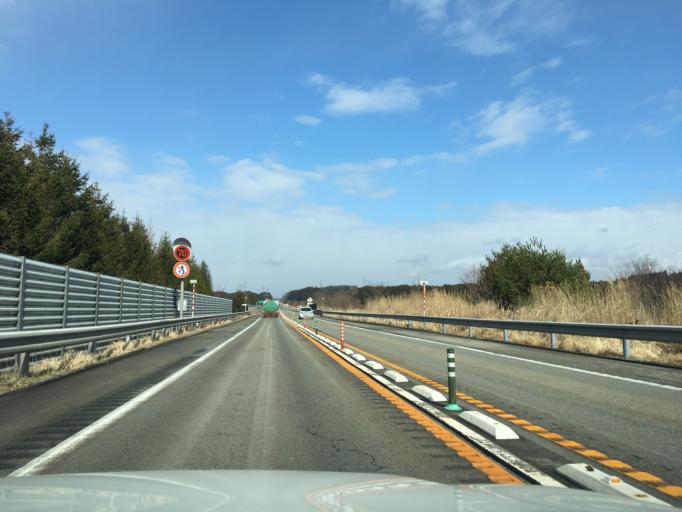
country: JP
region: Akita
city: Akita Shi
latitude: 39.7929
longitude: 140.1024
